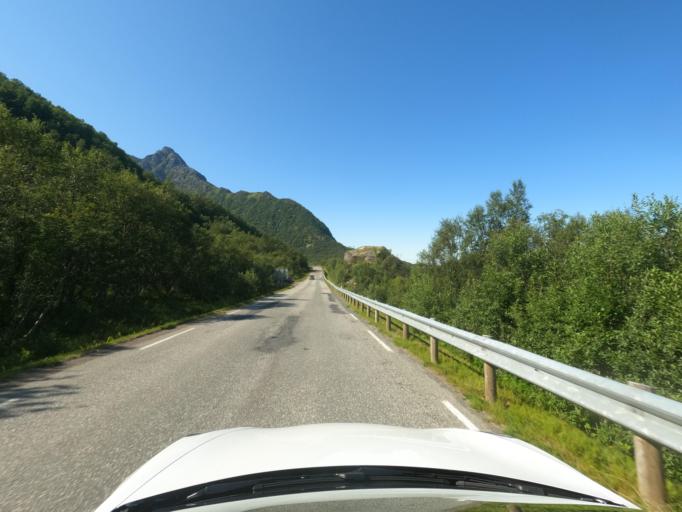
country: NO
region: Nordland
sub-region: Hadsel
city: Melbu
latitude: 68.4259
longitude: 14.8358
